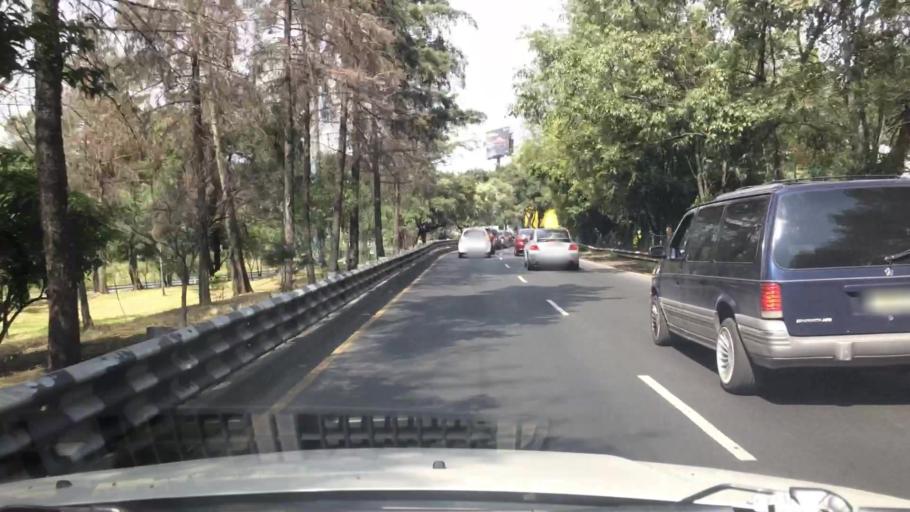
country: MX
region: Mexico City
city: Magdalena Contreras
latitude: 19.3041
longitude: -99.2058
